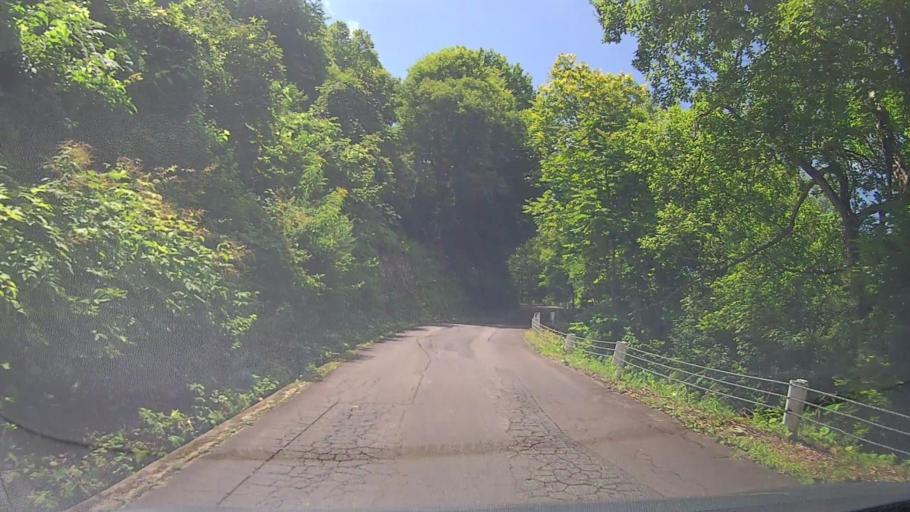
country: JP
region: Nagano
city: Iiyama
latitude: 36.9308
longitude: 138.4699
